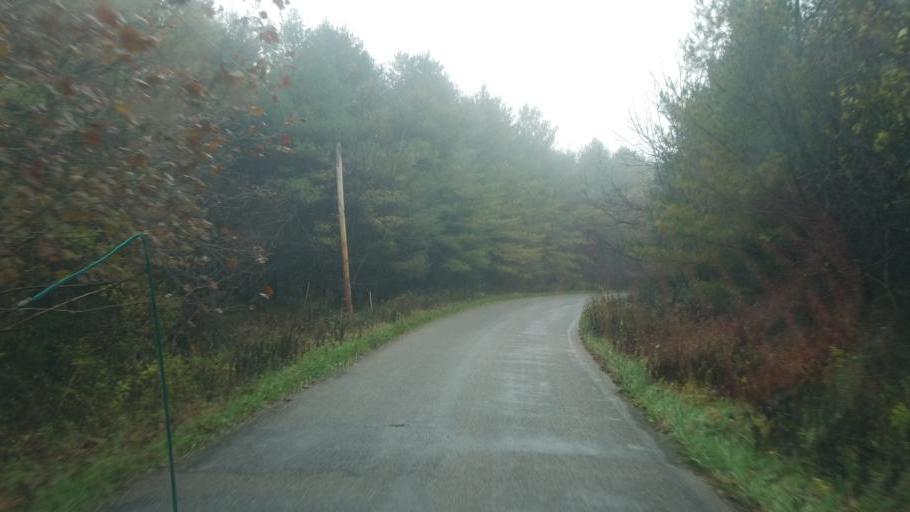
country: US
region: Ohio
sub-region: Athens County
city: Glouster
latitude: 39.4594
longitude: -81.9296
